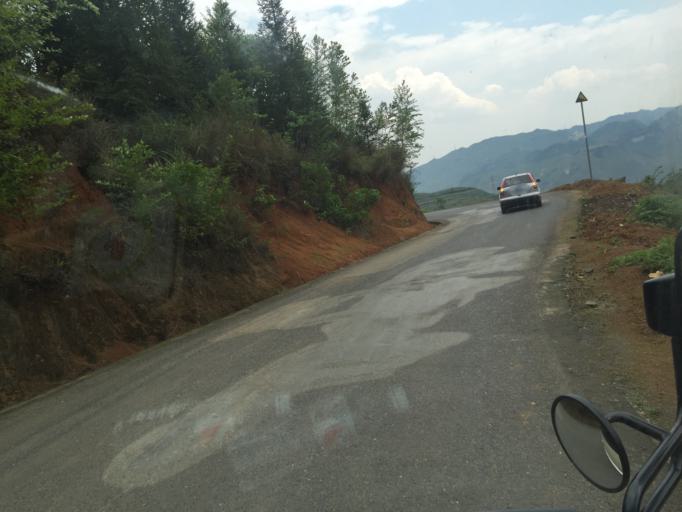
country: CN
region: Guangxi Zhuangzu Zizhiqu
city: Xinzhou
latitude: 25.6603
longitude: 105.2377
